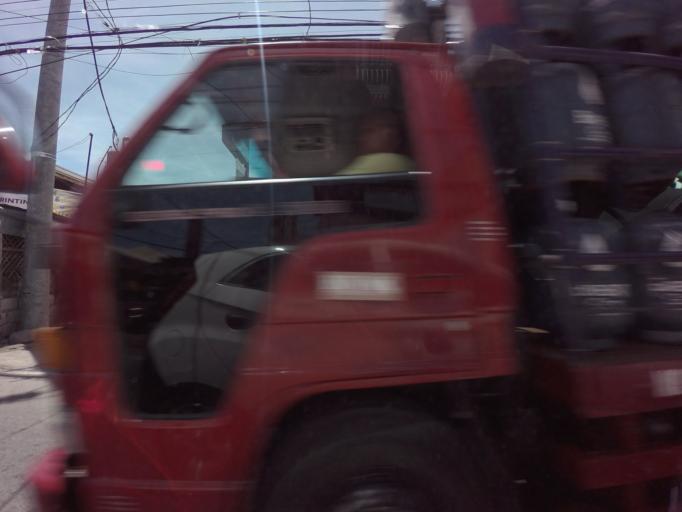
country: PH
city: Sambayanihan People's Village
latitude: 14.4566
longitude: 121.0531
